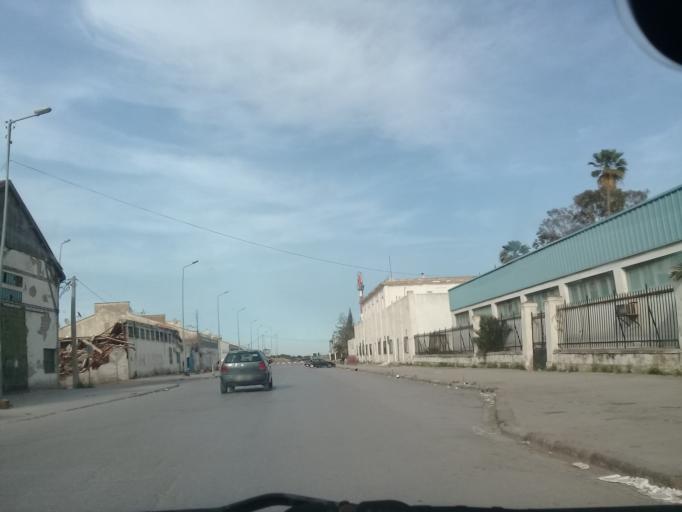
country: TN
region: Tunis
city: Tunis
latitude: 36.7930
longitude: 10.1878
